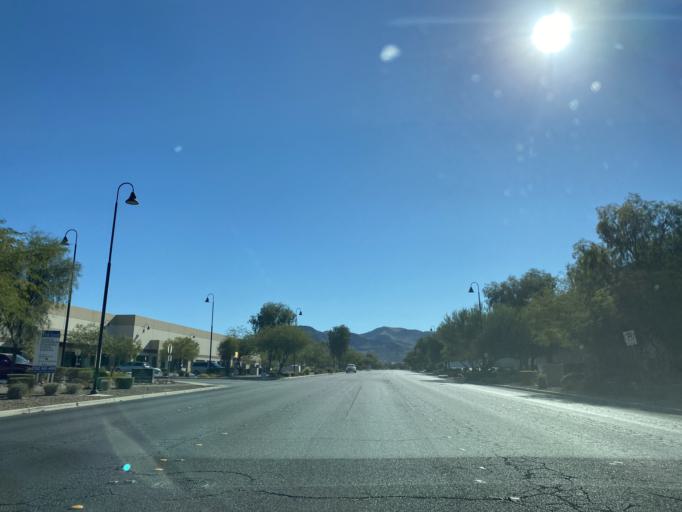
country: US
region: Nevada
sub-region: Clark County
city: Henderson
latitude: 36.0540
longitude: -115.0199
